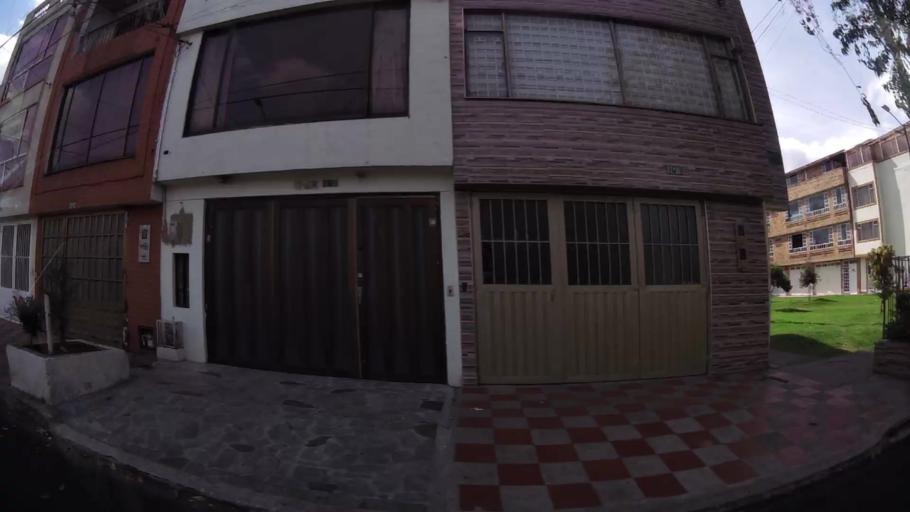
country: CO
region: Bogota D.C.
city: Bogota
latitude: 4.6442
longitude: -74.1349
